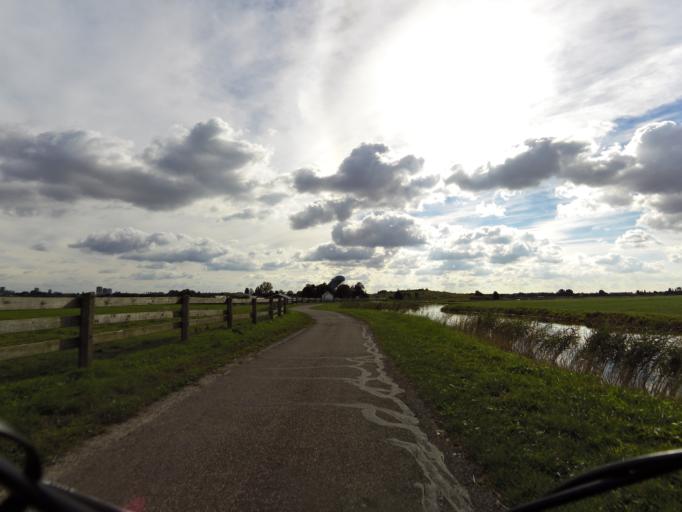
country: NL
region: South Holland
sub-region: Gemeente Zoetermeer
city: Zoetermeer
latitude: 52.0810
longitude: 4.4553
